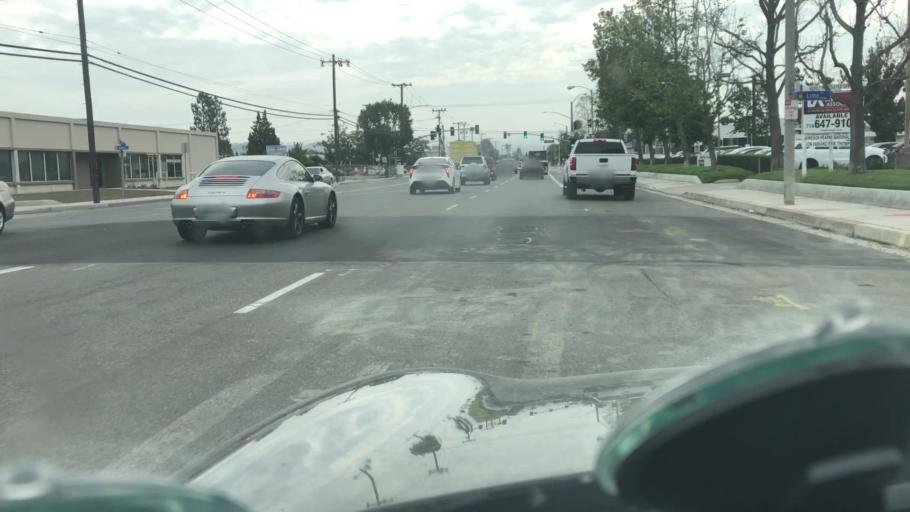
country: US
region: California
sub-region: Orange County
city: Orange
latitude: 33.8156
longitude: -117.8637
